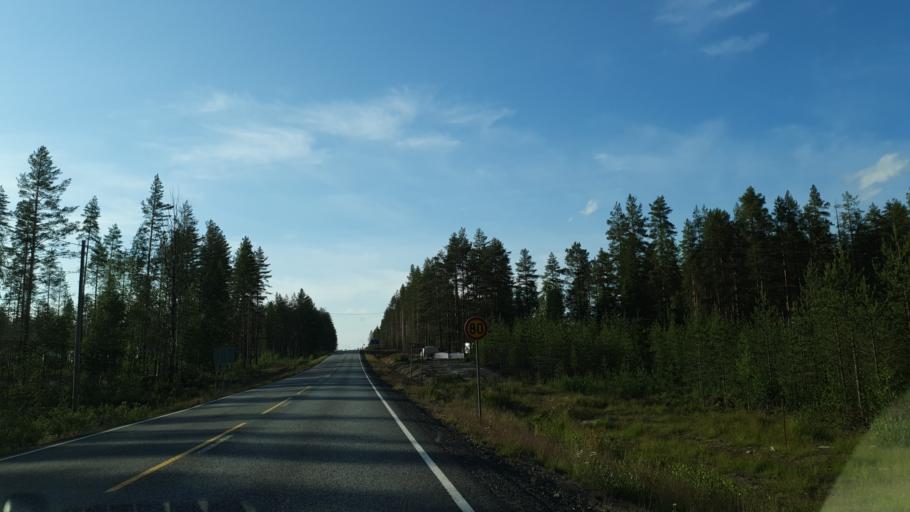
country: FI
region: Kainuu
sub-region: Kehys-Kainuu
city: Kuhmo
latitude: 64.0943
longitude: 29.4784
